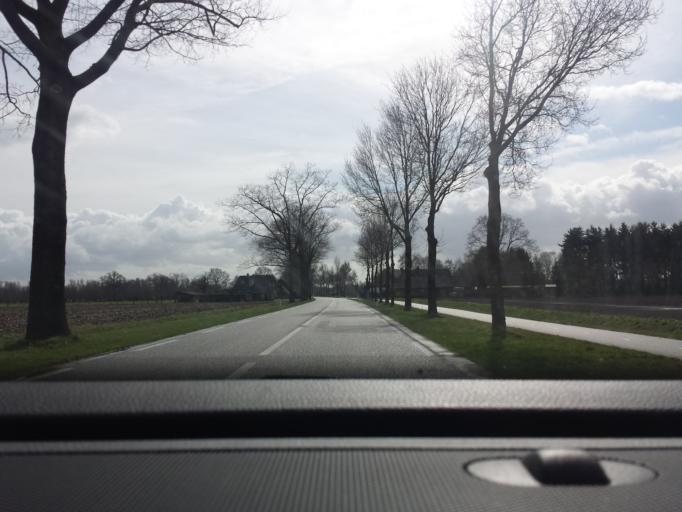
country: NL
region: Gelderland
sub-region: Oude IJsselstreek
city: Varsseveld
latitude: 51.9831
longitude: 6.4383
